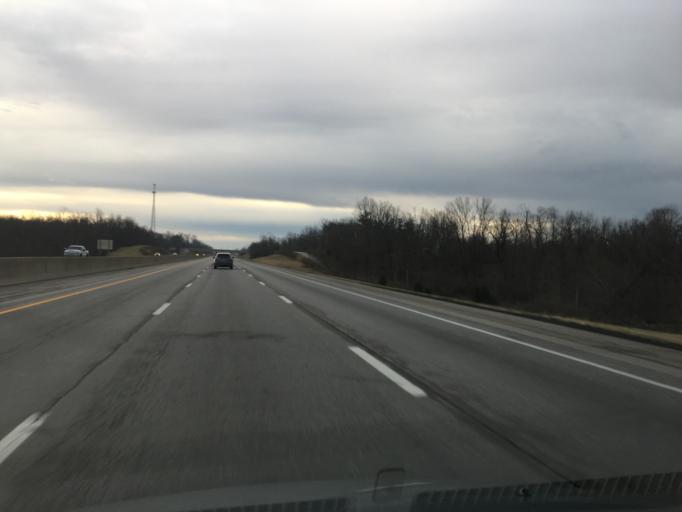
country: US
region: Kentucky
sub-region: Grant County
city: Crittenden
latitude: 38.7702
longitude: -84.6110
